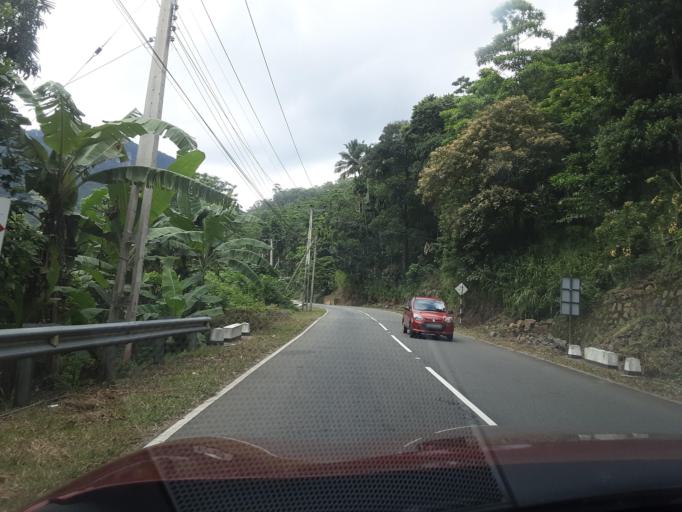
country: LK
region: Uva
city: Badulla
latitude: 6.9346
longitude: 81.1951
